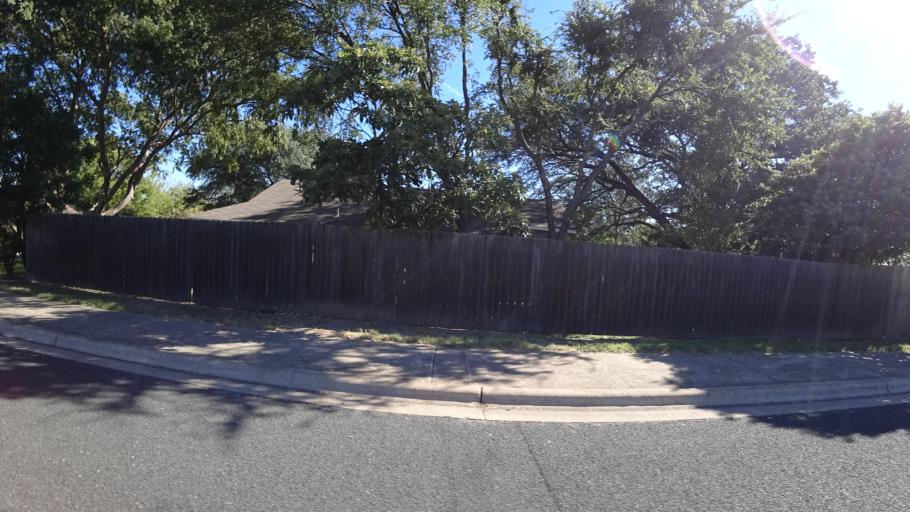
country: US
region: Texas
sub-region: Travis County
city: Austin
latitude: 30.2310
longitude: -97.7123
